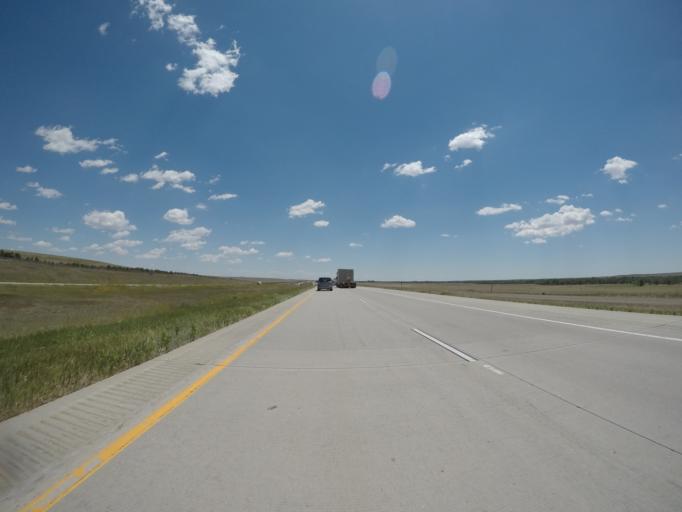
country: US
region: Colorado
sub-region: Lincoln County
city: Limon
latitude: 39.2807
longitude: -103.7689
